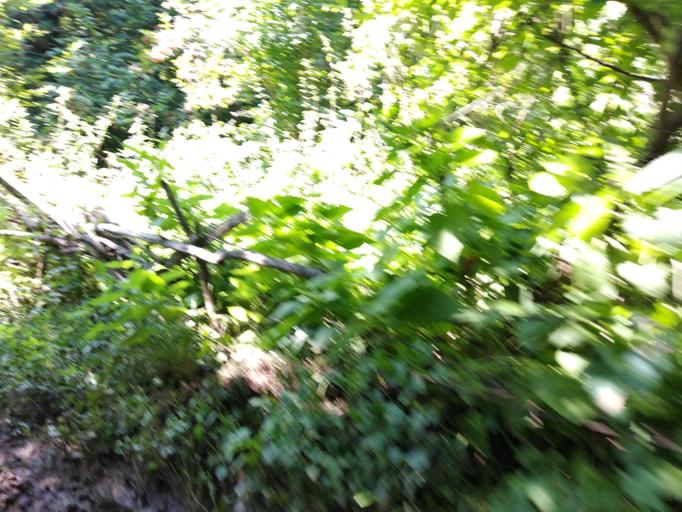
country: RU
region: Adygeya
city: Kamennomostskiy
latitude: 44.1982
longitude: 39.9565
